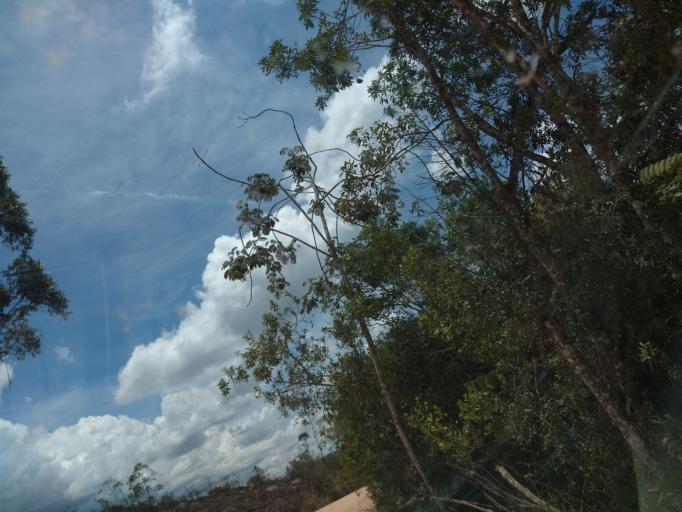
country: BR
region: Minas Gerais
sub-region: Sao Joao Del Rei
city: Sao Joao del Rei
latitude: -20.8940
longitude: -44.3060
